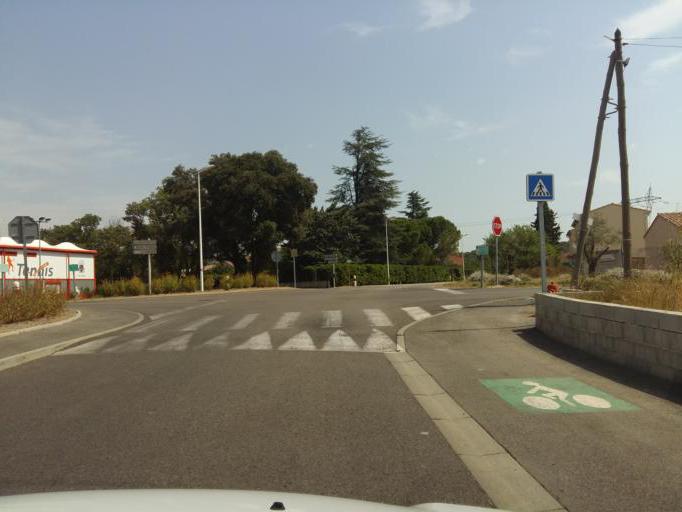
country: FR
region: Provence-Alpes-Cote d'Azur
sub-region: Departement du Vaucluse
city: Bollene
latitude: 44.2906
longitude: 4.7580
